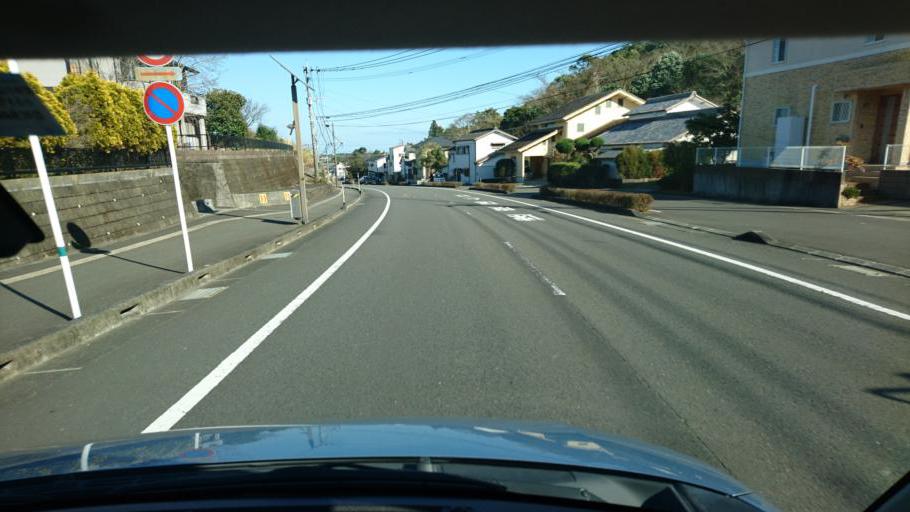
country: JP
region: Miyazaki
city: Miyazaki-shi
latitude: 31.8323
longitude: 131.4316
